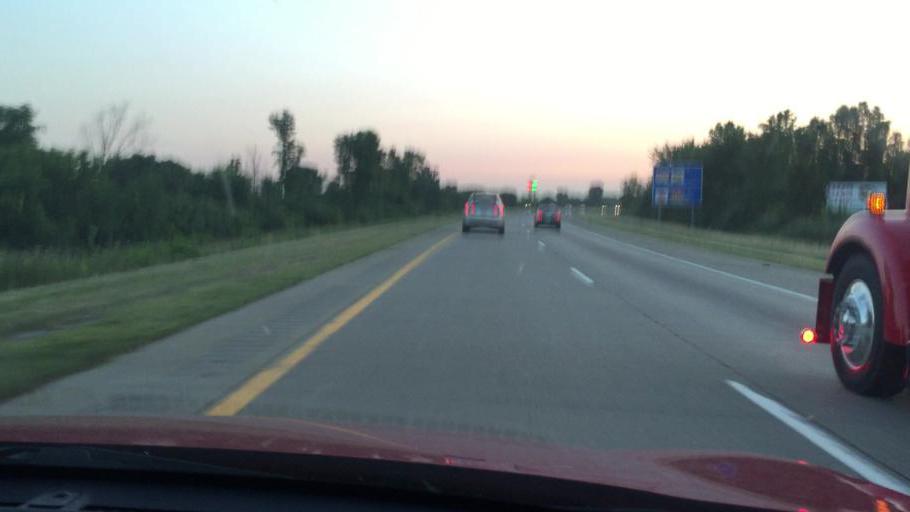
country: US
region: Michigan
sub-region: Monroe County
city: Lambertville
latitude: 41.7898
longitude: -83.6947
